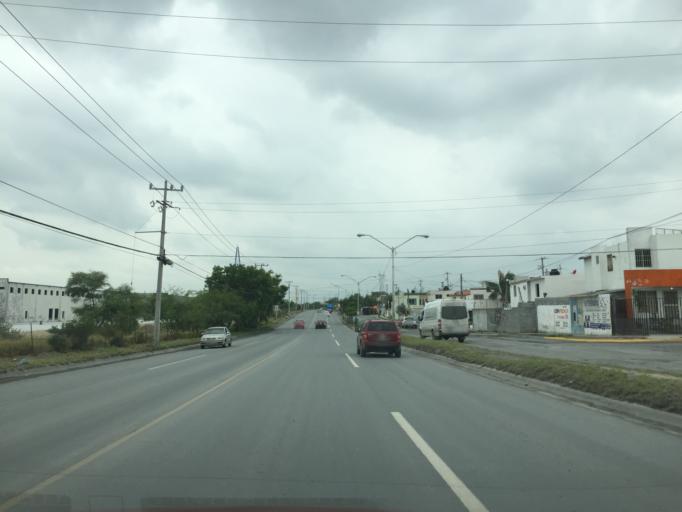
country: MX
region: Nuevo Leon
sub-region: Apodaca
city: Fraccionamiento Cosmopolis Octavo Sector
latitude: 25.8279
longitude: -100.2446
